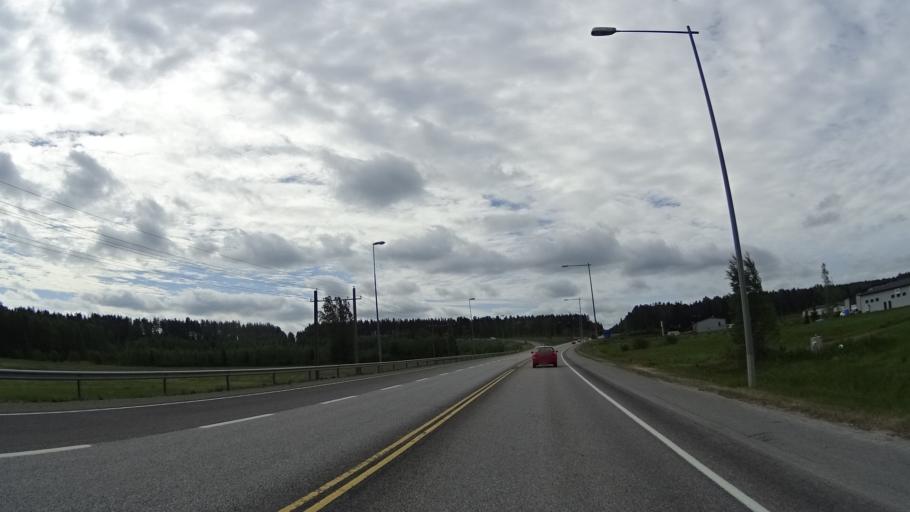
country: FI
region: Uusimaa
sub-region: Helsinki
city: Vihti
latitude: 60.3576
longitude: 24.3267
